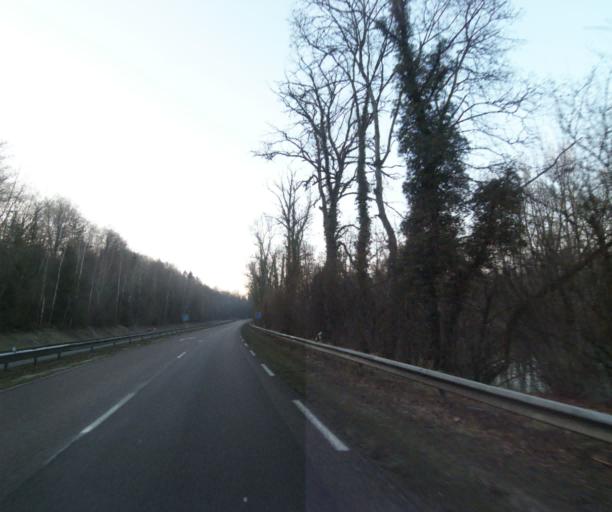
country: FR
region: Lorraine
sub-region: Departement de la Meuse
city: Ancerville
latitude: 48.6119
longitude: 5.0037
